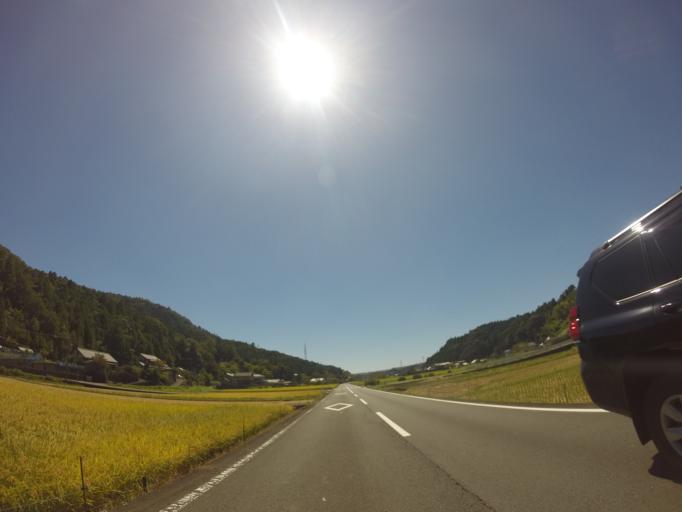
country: JP
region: Shizuoka
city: Kanaya
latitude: 34.8692
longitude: 138.1334
